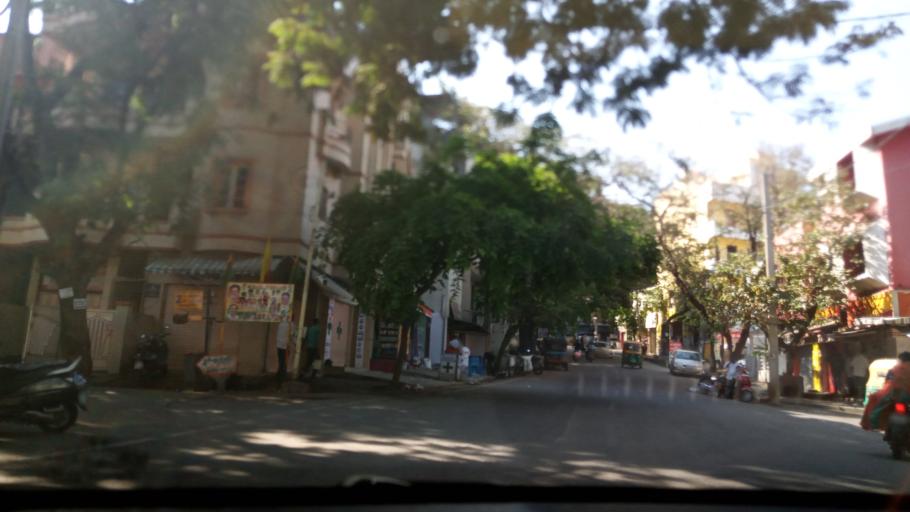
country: IN
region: Karnataka
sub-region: Bangalore Urban
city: Bangalore
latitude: 13.0123
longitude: 77.5451
